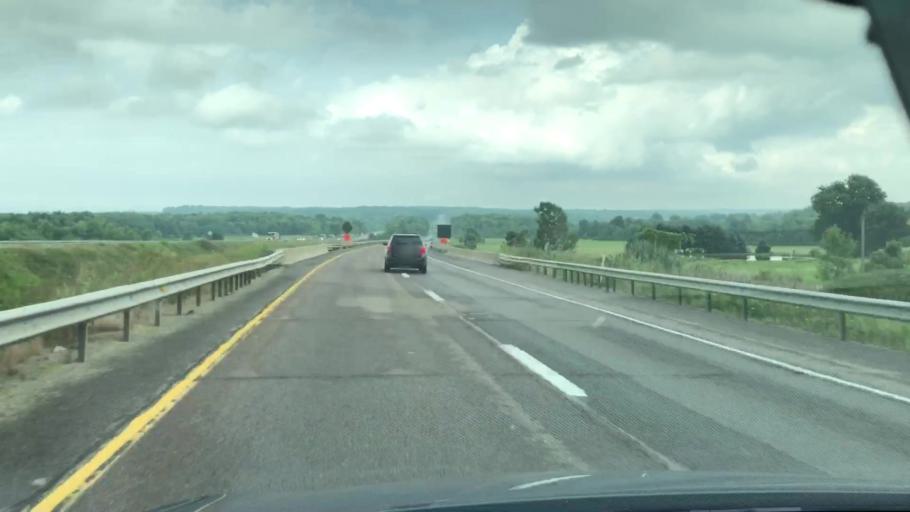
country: US
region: Pennsylvania
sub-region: Erie County
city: Fairview
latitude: 41.9845
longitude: -80.1752
